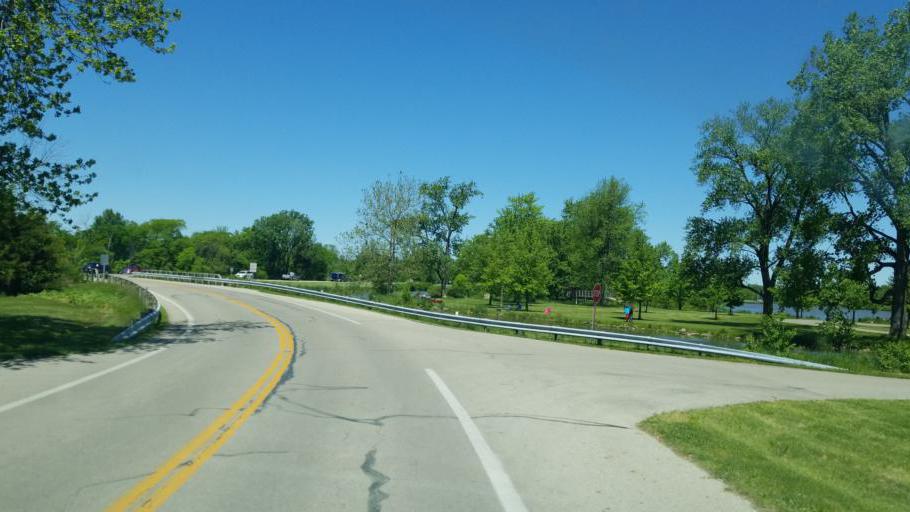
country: US
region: Ohio
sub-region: Shelby County
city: Fort Loramie
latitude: 40.3596
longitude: -84.3592
